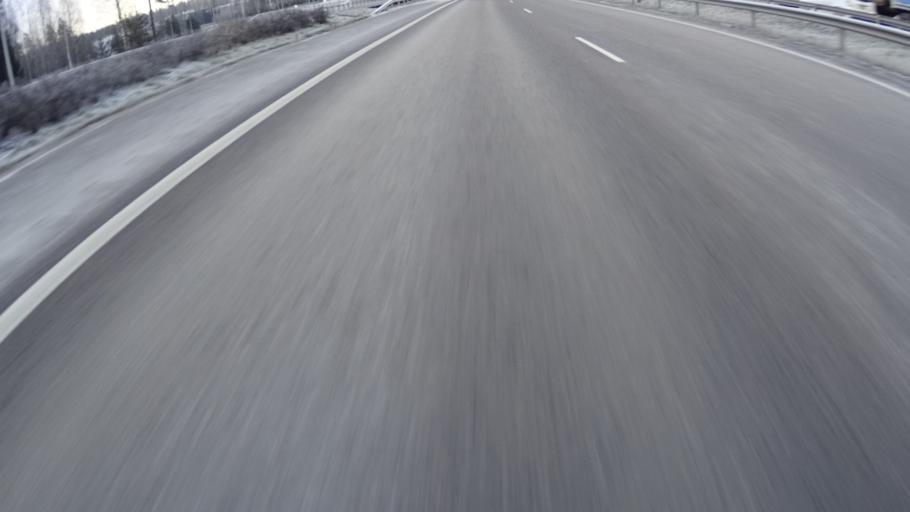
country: FI
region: Uusimaa
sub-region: Helsinki
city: Kilo
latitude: 60.3094
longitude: 24.8446
